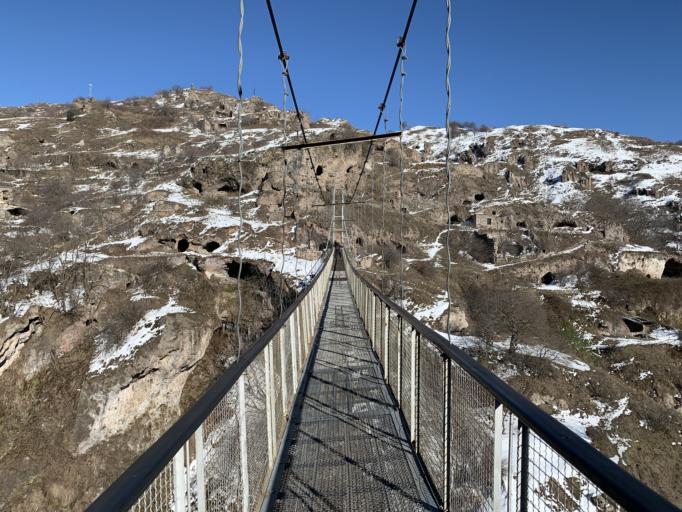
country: AM
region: Syunik'i Marz
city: Khndzoresk
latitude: 39.5007
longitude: 46.4330
